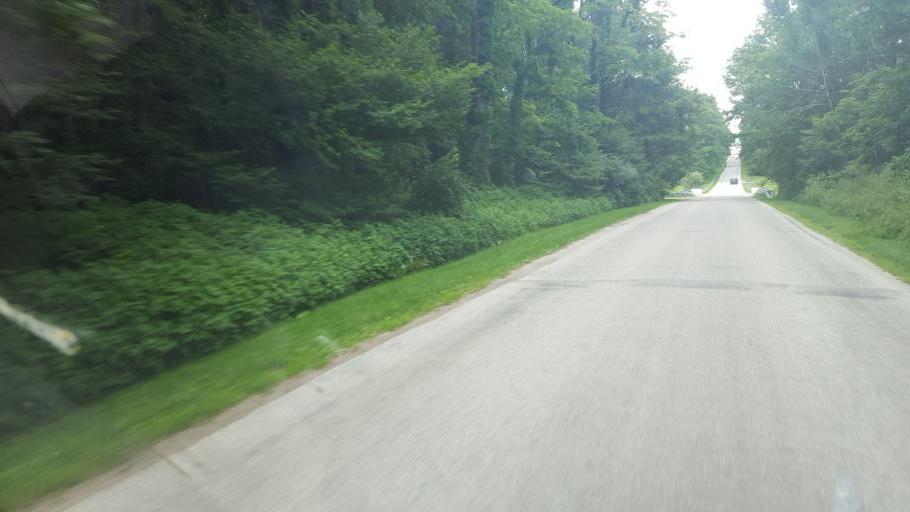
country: US
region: Ohio
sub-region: Richland County
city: Lexington
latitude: 40.7087
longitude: -82.6562
